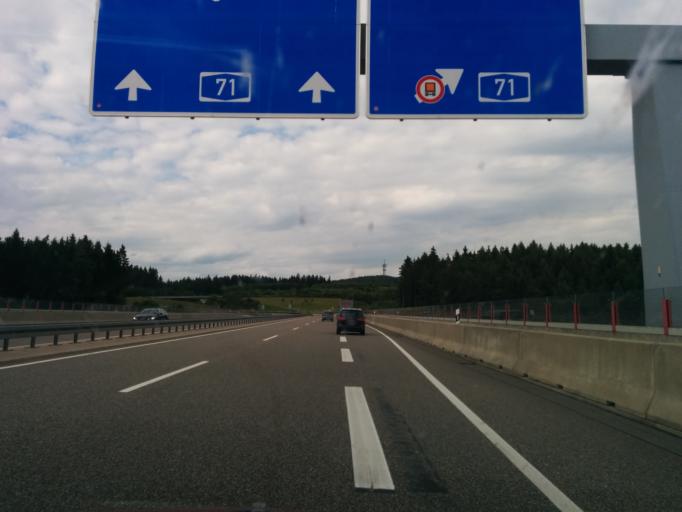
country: DE
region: Thuringia
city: Suhl
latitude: 50.6044
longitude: 10.6451
